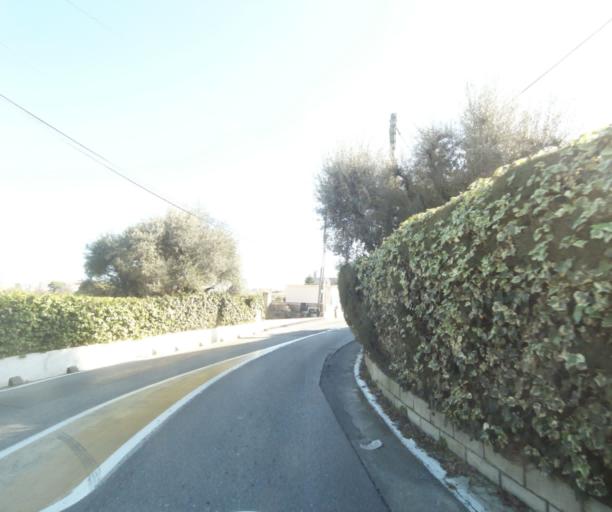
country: FR
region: Provence-Alpes-Cote d'Azur
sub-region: Departement des Alpes-Maritimes
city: Biot
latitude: 43.6041
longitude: 7.1077
